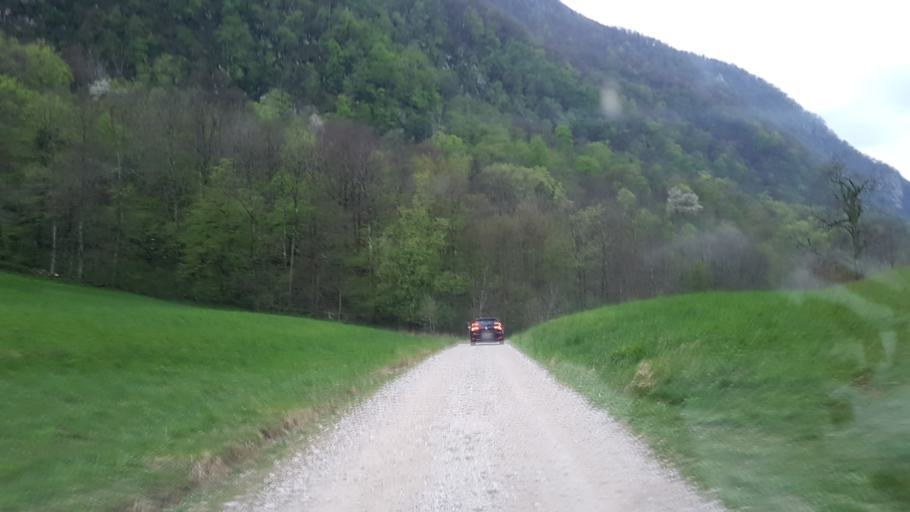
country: SI
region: Kobarid
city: Kobarid
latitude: 46.2405
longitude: 13.5358
